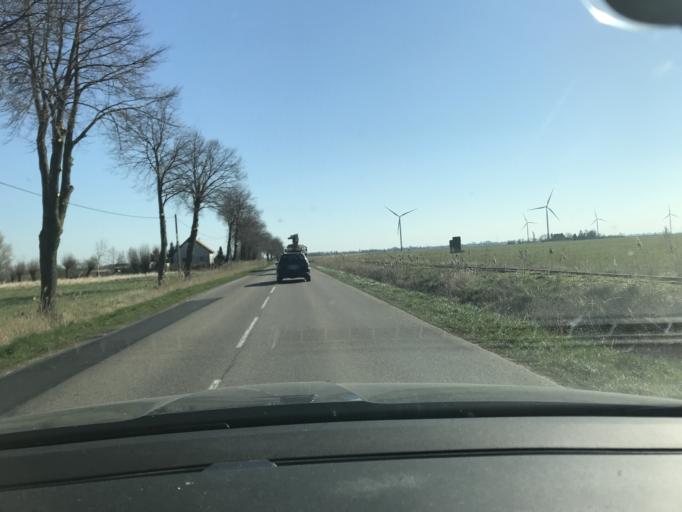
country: PL
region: Pomeranian Voivodeship
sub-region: Powiat nowodworski
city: Nowy Dwor Gdanski
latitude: 54.2641
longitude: 19.1359
